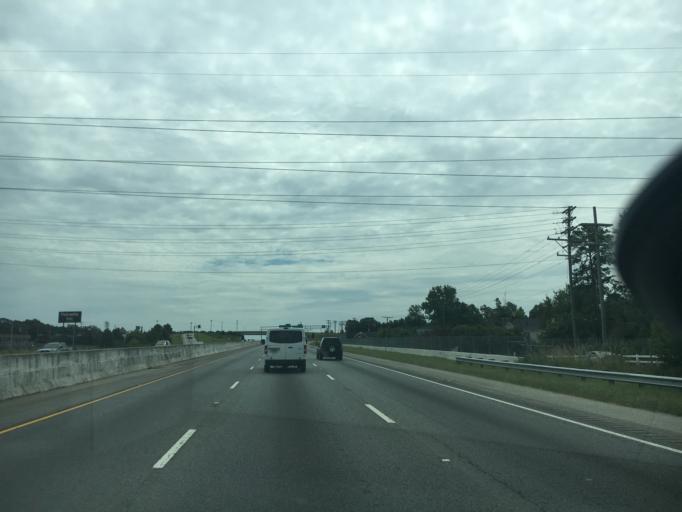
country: US
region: South Carolina
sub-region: Greenville County
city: Simpsonville
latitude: 34.7235
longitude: -82.2592
